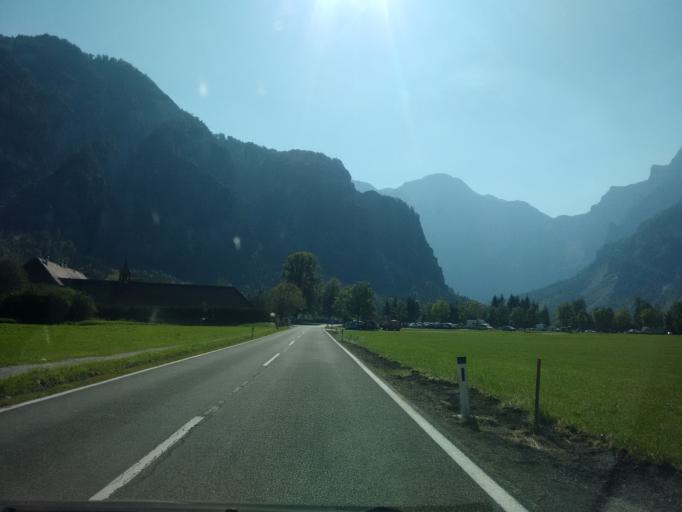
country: AT
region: Upper Austria
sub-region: Politischer Bezirk Gmunden
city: Gruenau im Almtal
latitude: 47.7449
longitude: 13.9508
